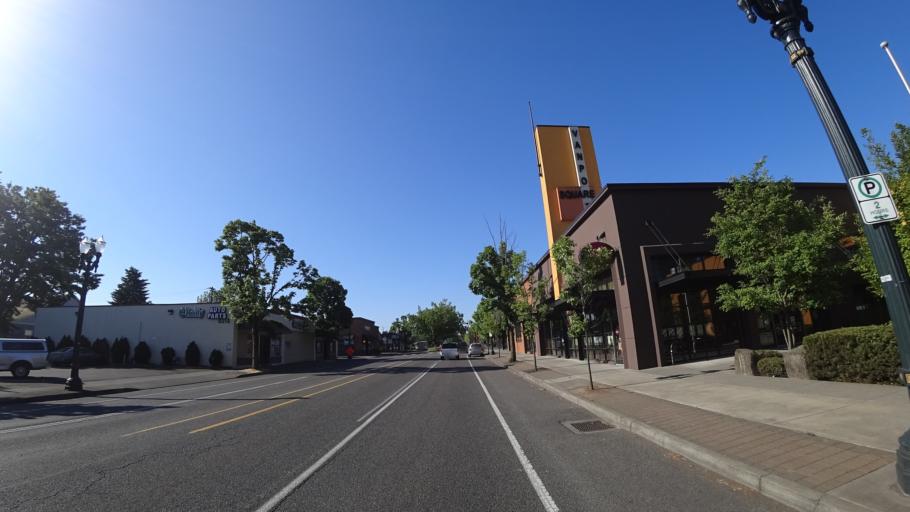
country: US
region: Oregon
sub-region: Multnomah County
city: Portland
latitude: 45.5612
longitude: -122.6616
